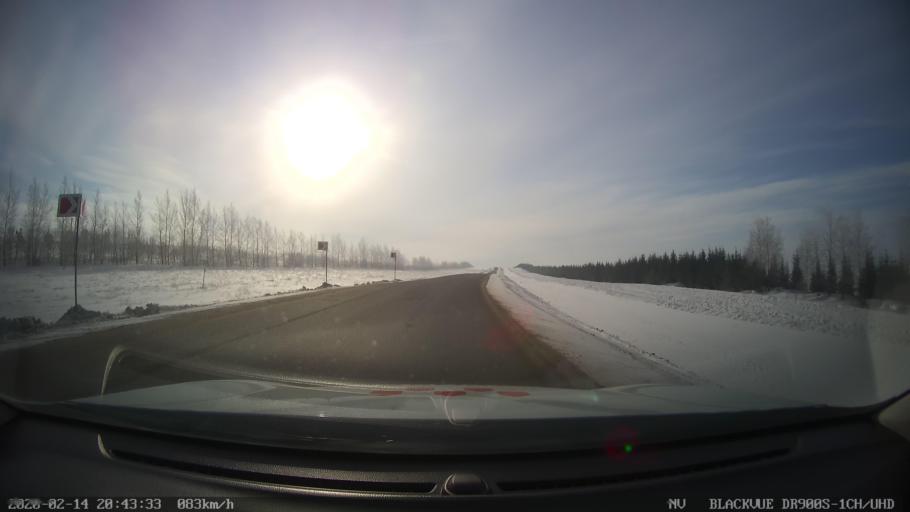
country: RU
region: Tatarstan
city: Kuybyshevskiy Zaton
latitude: 55.3068
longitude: 49.1484
